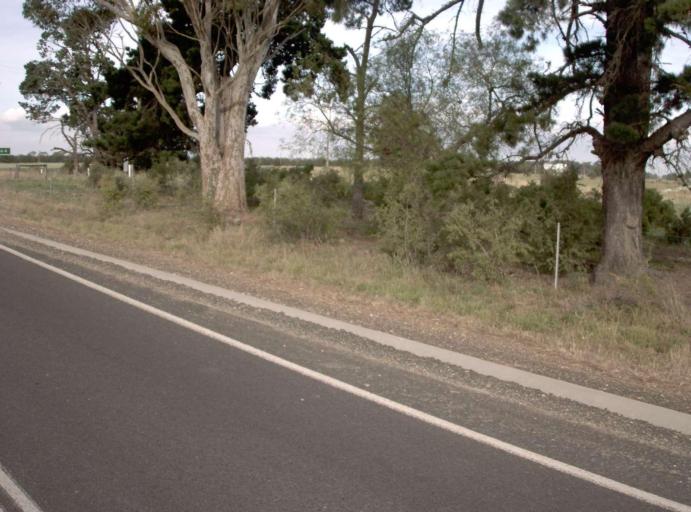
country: AU
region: Victoria
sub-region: Wellington
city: Heyfield
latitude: -38.0093
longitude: 146.7791
